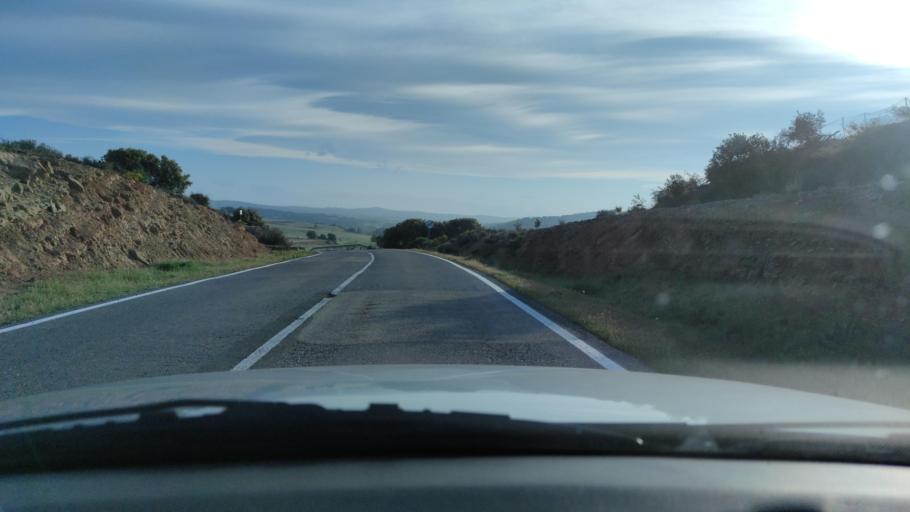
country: ES
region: Catalonia
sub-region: Provincia de Lleida
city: Agramunt
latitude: 41.8251
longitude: 1.0597
